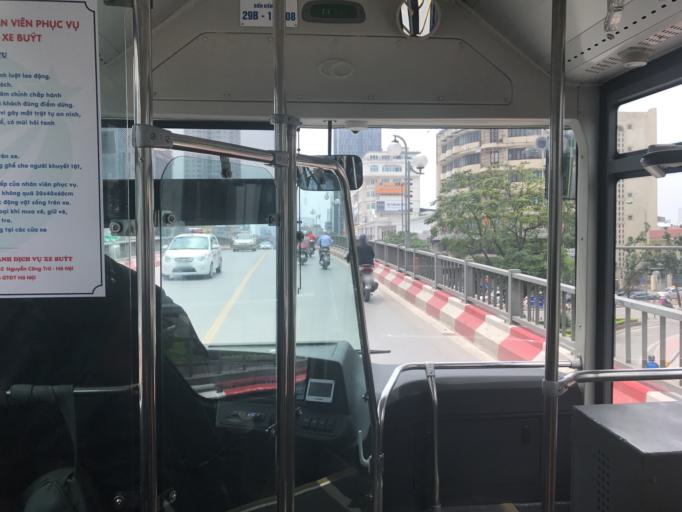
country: VN
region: Ha Noi
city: Dong Da
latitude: 21.0171
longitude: 105.8153
